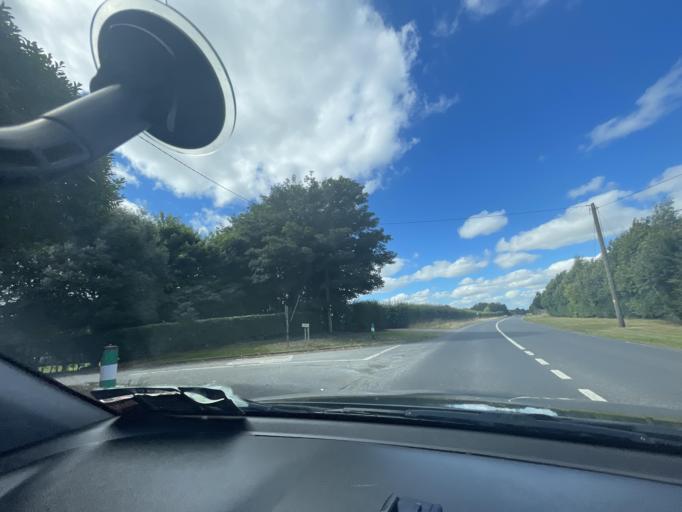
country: IE
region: Leinster
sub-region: An Mhi
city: Dunshaughlin
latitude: 53.5187
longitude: -6.6412
